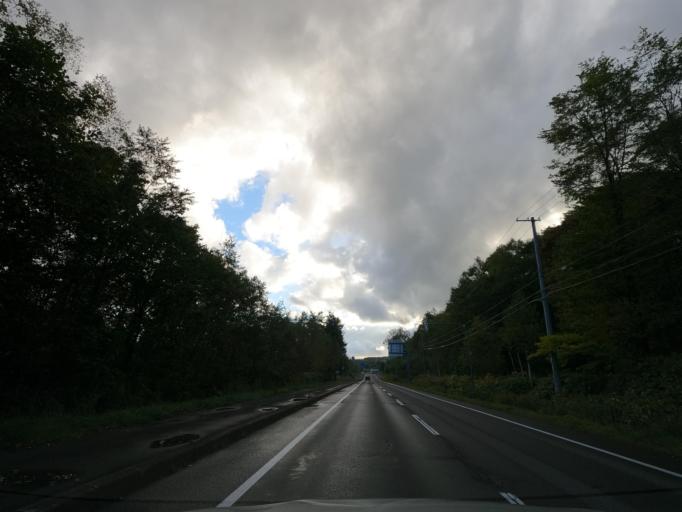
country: JP
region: Hokkaido
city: Shiraoi
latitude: 42.6761
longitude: 141.0872
